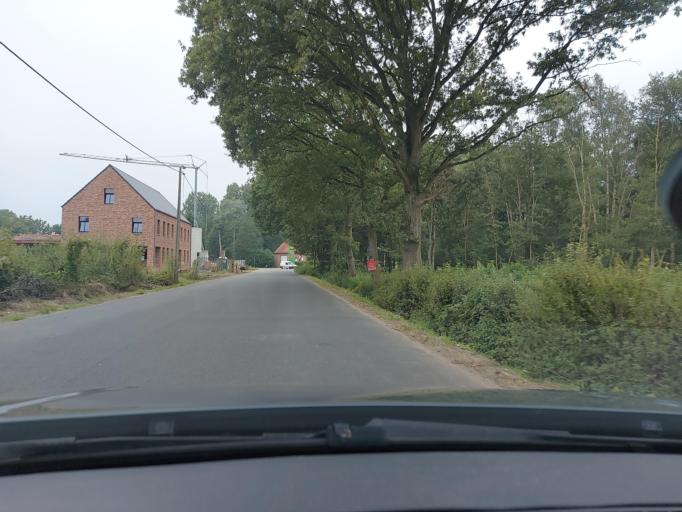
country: BE
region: Flanders
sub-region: Provincie Antwerpen
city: Meerhout
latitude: 51.1652
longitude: 5.0402
